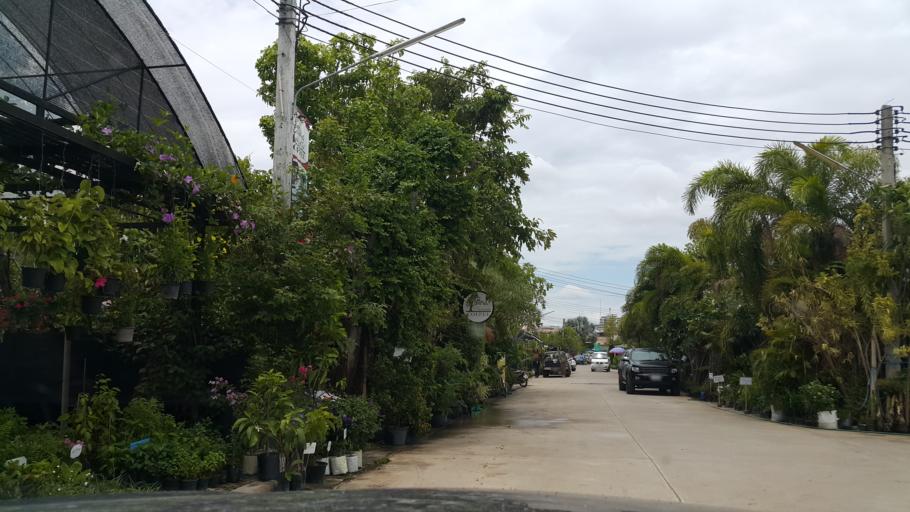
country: TH
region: Chiang Mai
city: Chiang Mai
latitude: 18.8065
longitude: 98.9993
